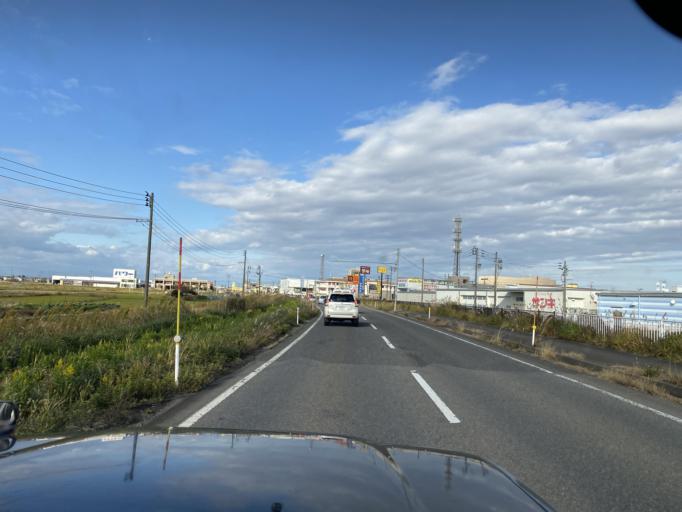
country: JP
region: Niigata
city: Niitsu-honcho
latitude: 37.7841
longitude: 139.1118
